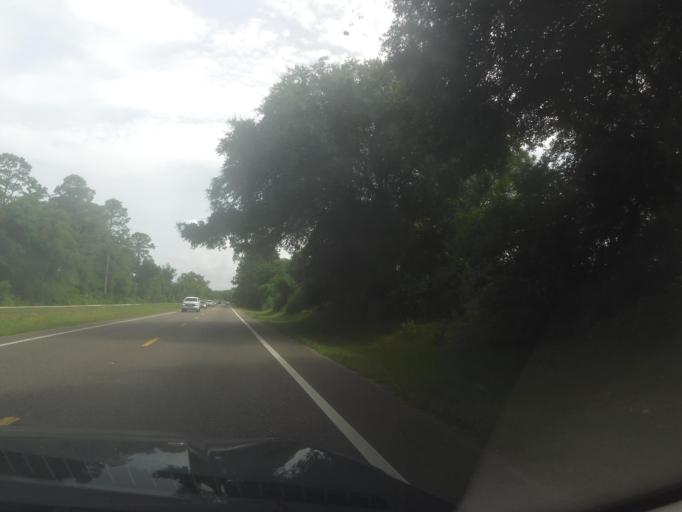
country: US
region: Florida
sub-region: Saint Johns County
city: Saint Augustine
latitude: 29.9048
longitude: -81.3610
